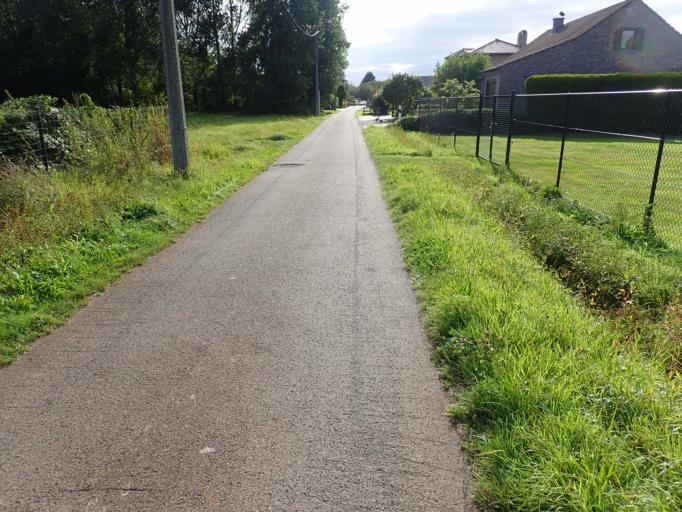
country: BE
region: Flanders
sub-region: Provincie Antwerpen
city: Nijlen
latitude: 51.1536
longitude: 4.6765
